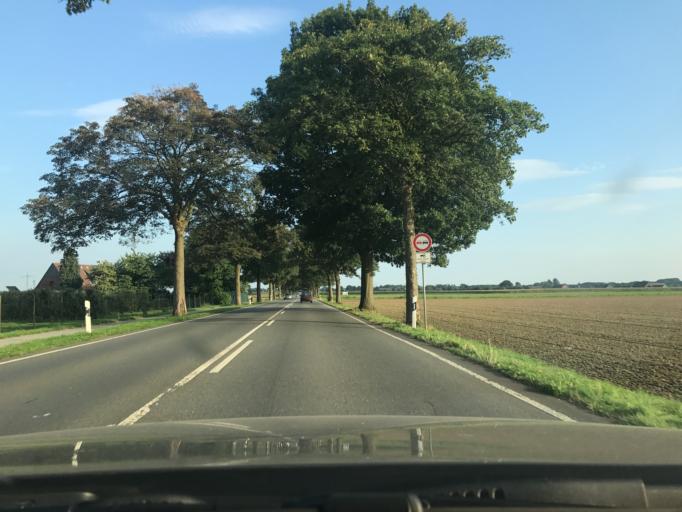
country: DE
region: North Rhine-Westphalia
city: Geldern
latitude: 51.4754
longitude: 6.3483
